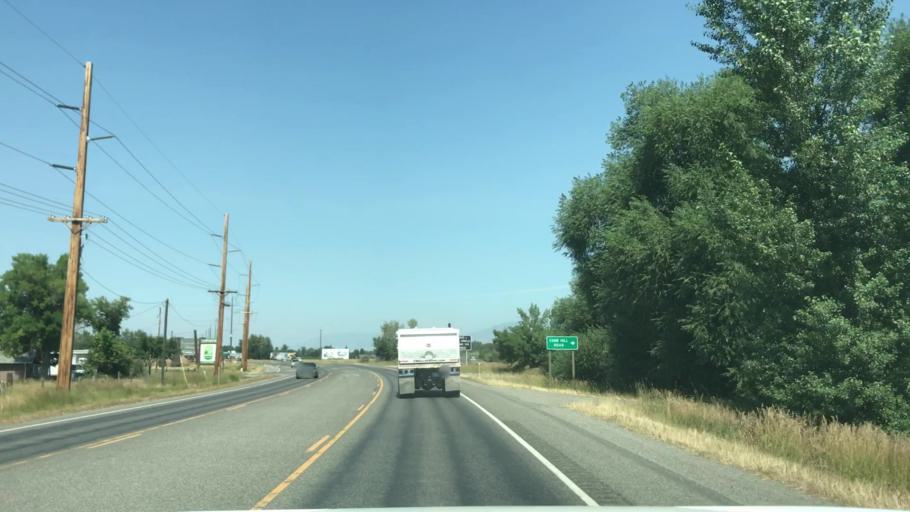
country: US
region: Montana
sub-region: Gallatin County
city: Four Corners
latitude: 45.6580
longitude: -111.1863
